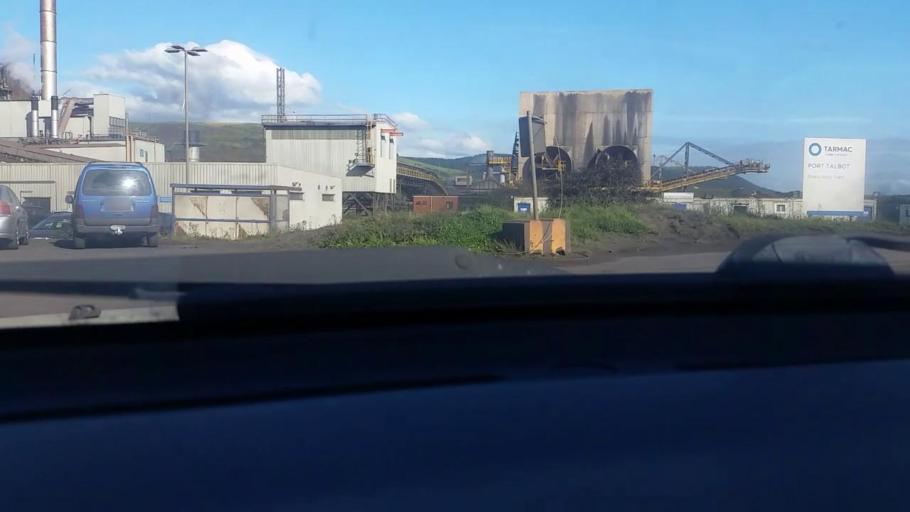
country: GB
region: Wales
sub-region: Neath Port Talbot
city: Taibach
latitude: 51.5753
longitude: -3.7786
